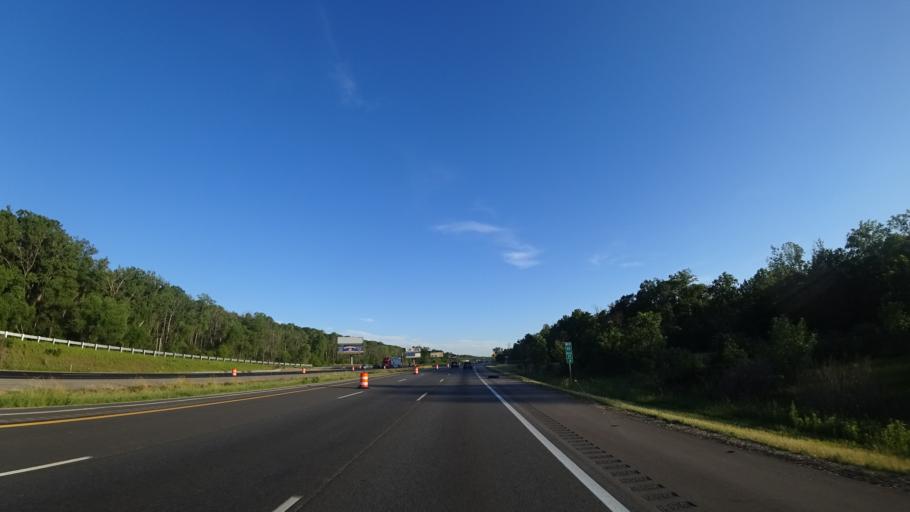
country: US
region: Michigan
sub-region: Berrien County
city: Stevensville
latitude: 42.0092
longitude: -86.5331
